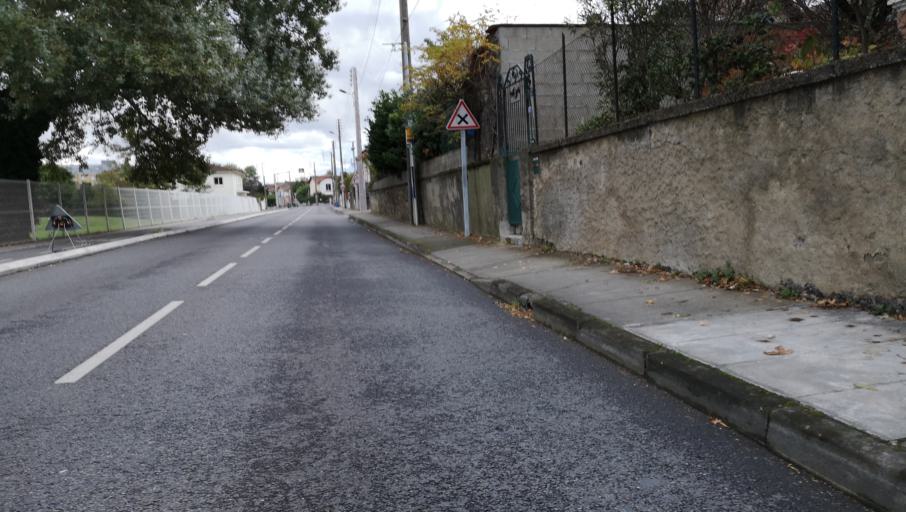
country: FR
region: Midi-Pyrenees
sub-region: Departement de la Haute-Garonne
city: Blagnac
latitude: 43.6096
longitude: 1.4060
